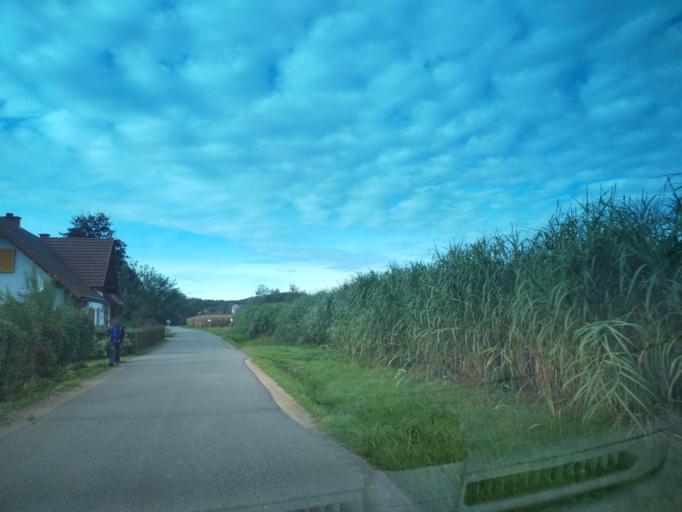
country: AT
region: Styria
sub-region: Politischer Bezirk Leibnitz
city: Sankt Johann im Saggautal
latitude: 46.6963
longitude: 15.3920
